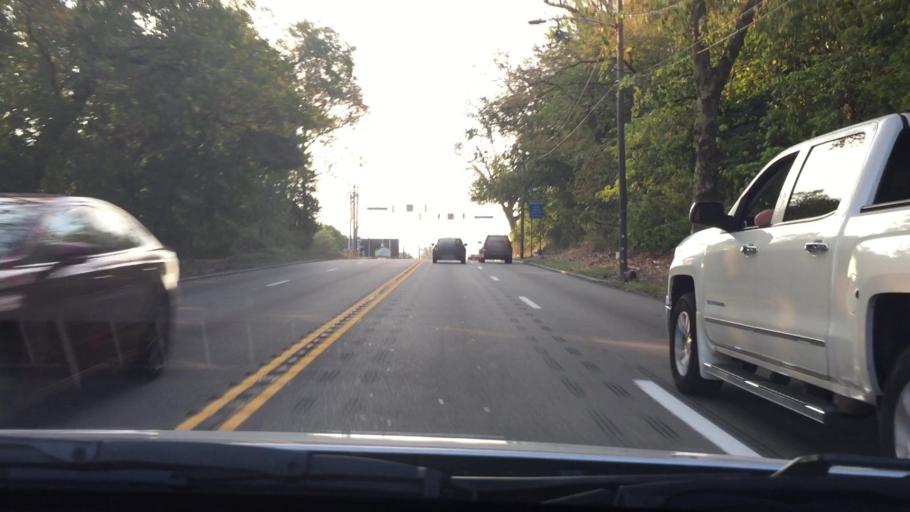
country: US
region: Pennsylvania
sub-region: Allegheny County
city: Bellevue
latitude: 40.4857
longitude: -80.0531
